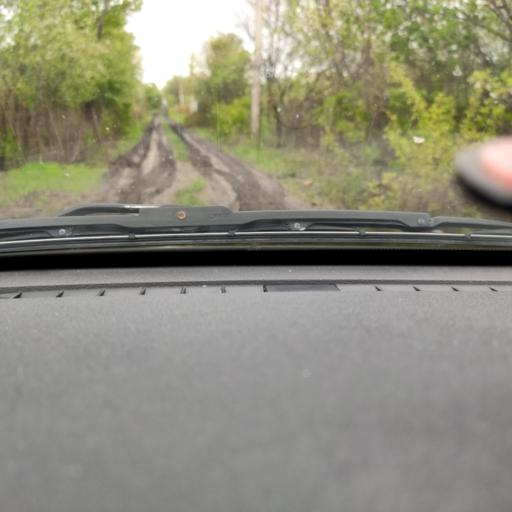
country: RU
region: Voronezj
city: Maslovka
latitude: 51.4901
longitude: 39.2190
